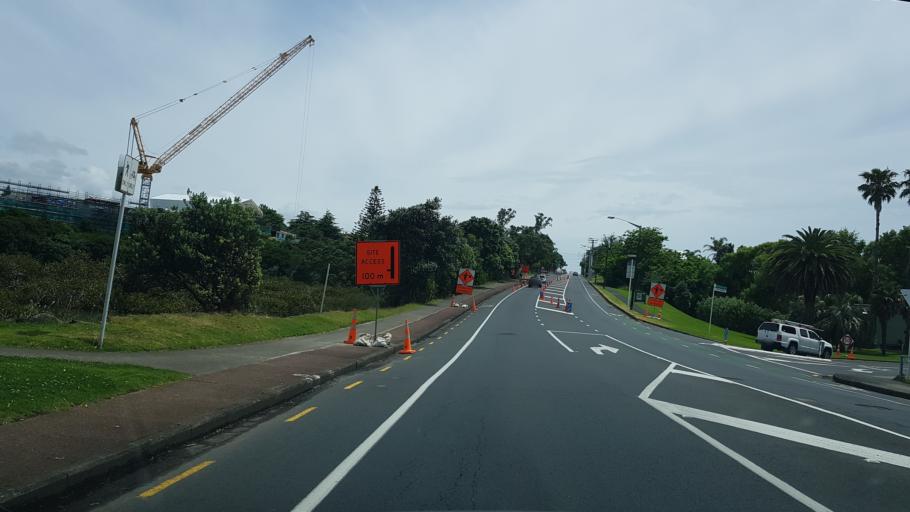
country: NZ
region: Auckland
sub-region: Auckland
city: North Shore
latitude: -36.8182
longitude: 174.7949
